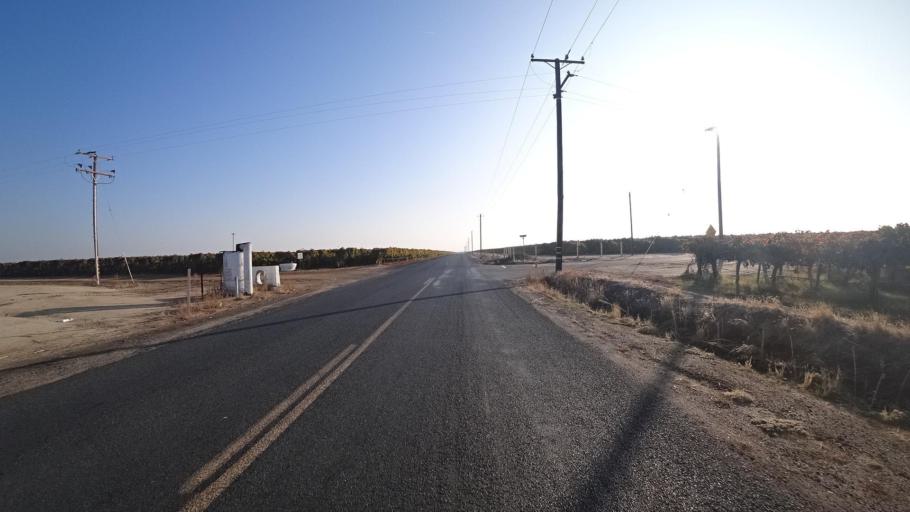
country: US
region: California
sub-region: Tulare County
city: Richgrove
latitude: 35.7906
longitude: -119.1344
